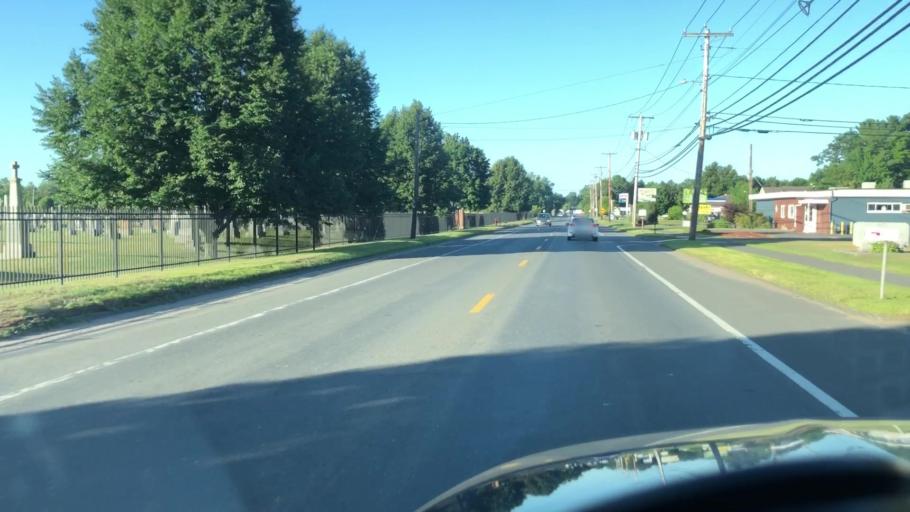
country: US
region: Massachusetts
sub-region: Hampden County
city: Westfield
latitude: 42.1476
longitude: -72.7292
